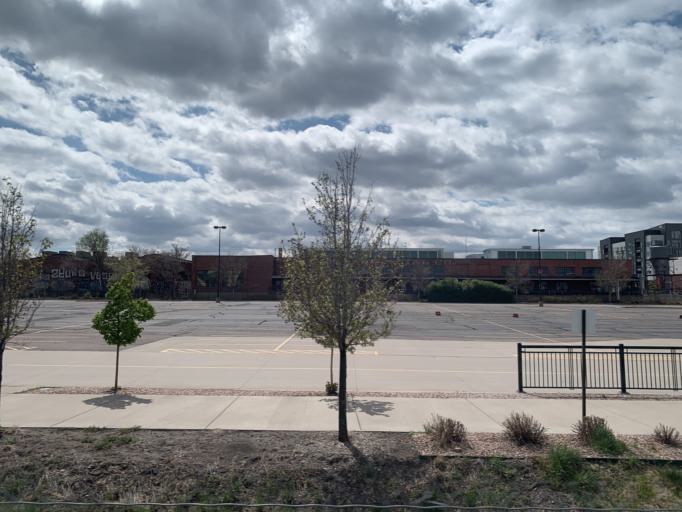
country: US
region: Colorado
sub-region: Denver County
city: Denver
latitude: 39.7642
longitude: -104.9842
